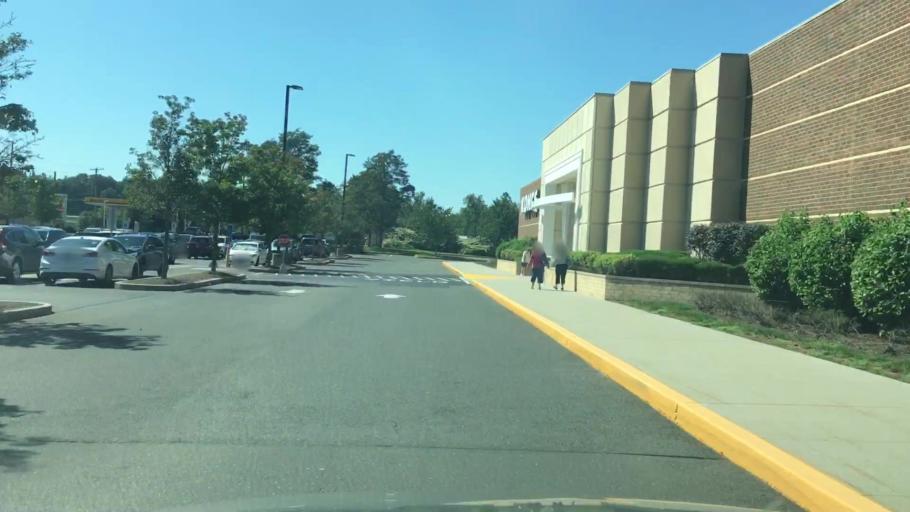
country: US
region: Connecticut
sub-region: Hartford County
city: Manchester
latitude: 41.8138
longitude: -72.5112
